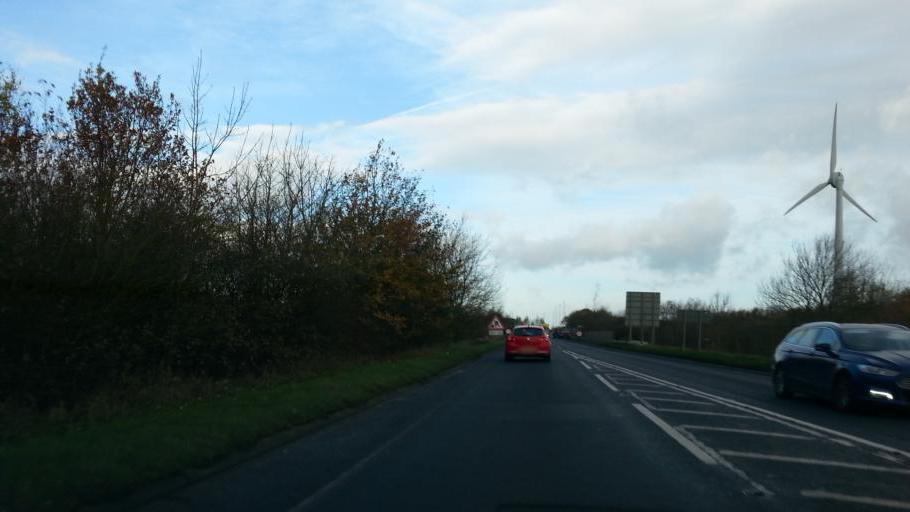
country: GB
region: England
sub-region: Leicestershire
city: Ashby de la Zouch
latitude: 52.7457
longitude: -1.4422
